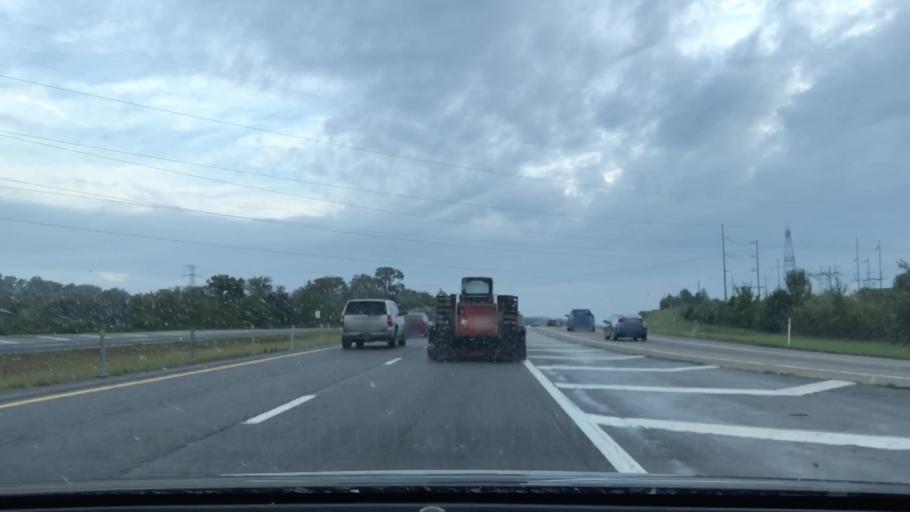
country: US
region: Tennessee
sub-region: Sumner County
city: Shackle Island
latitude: 36.3597
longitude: -86.5314
